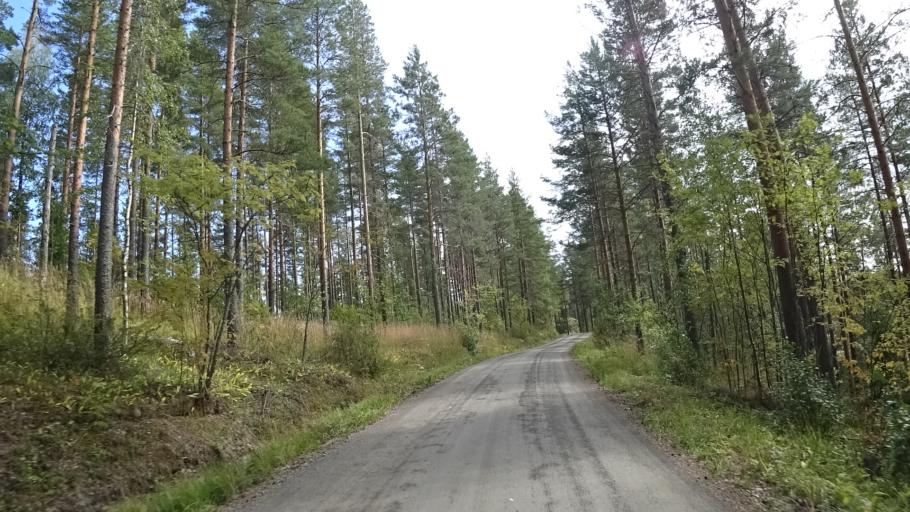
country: FI
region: North Karelia
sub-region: Joensuu
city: Pyhaeselkae
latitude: 62.3748
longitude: 29.8165
